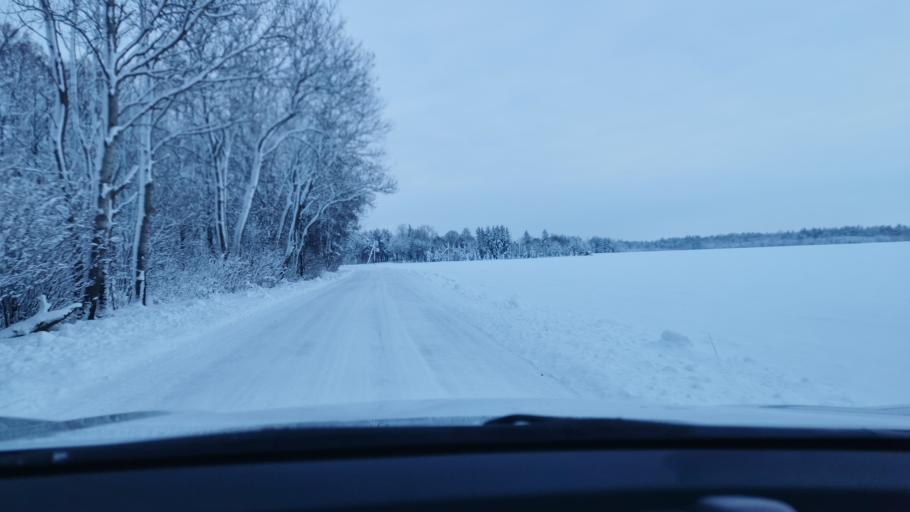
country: EE
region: Laeaene-Virumaa
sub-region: Haljala vald
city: Haljala
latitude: 59.5055
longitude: 26.2871
